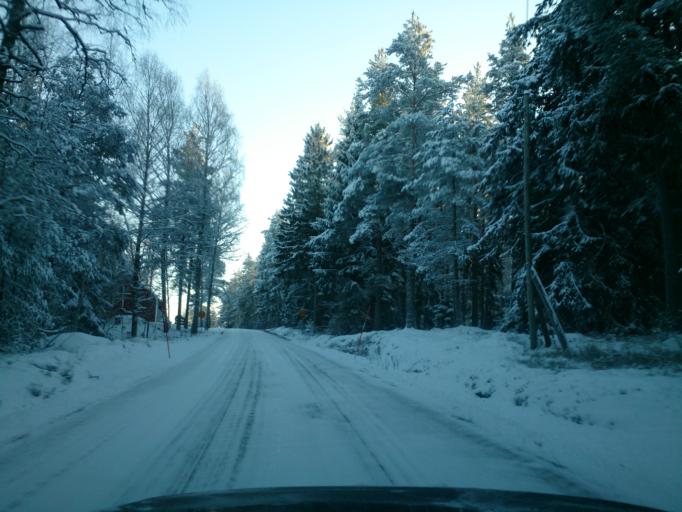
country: SE
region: OEstergoetland
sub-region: Norrkopings Kommun
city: Krokek
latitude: 58.4962
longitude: 16.5498
